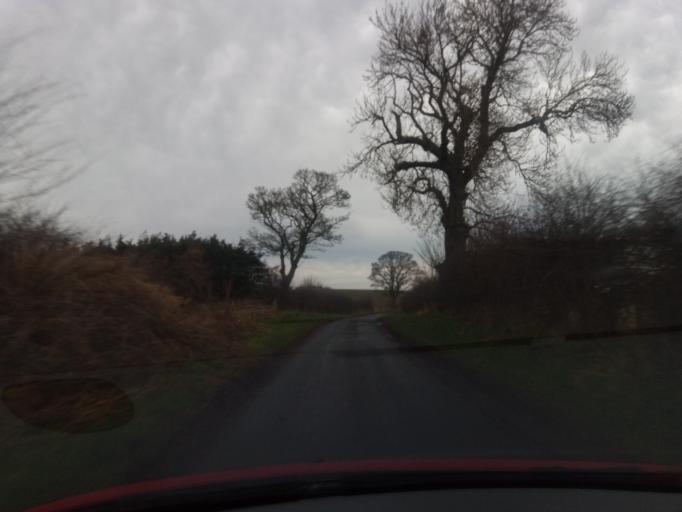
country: GB
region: England
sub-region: Northumberland
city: Wooler
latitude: 55.5009
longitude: -1.9399
